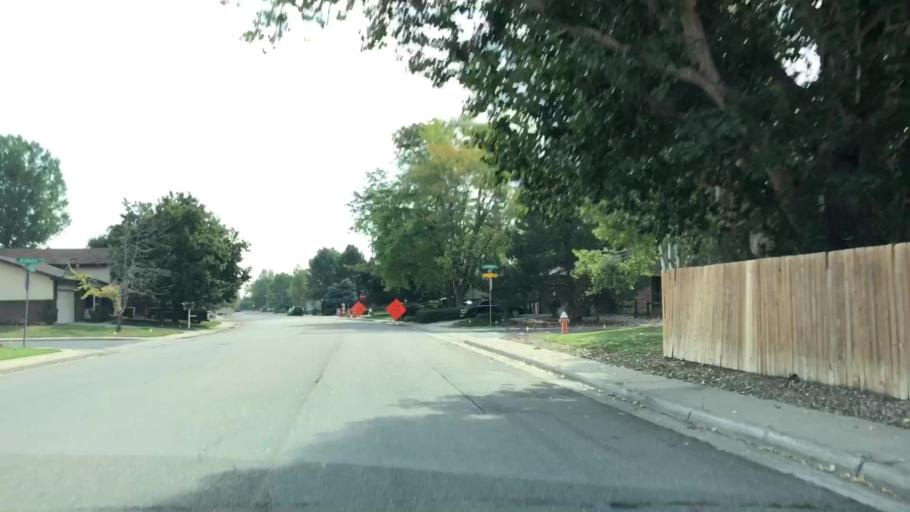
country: US
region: Colorado
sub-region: Larimer County
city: Loveland
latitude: 40.4158
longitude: -105.0550
